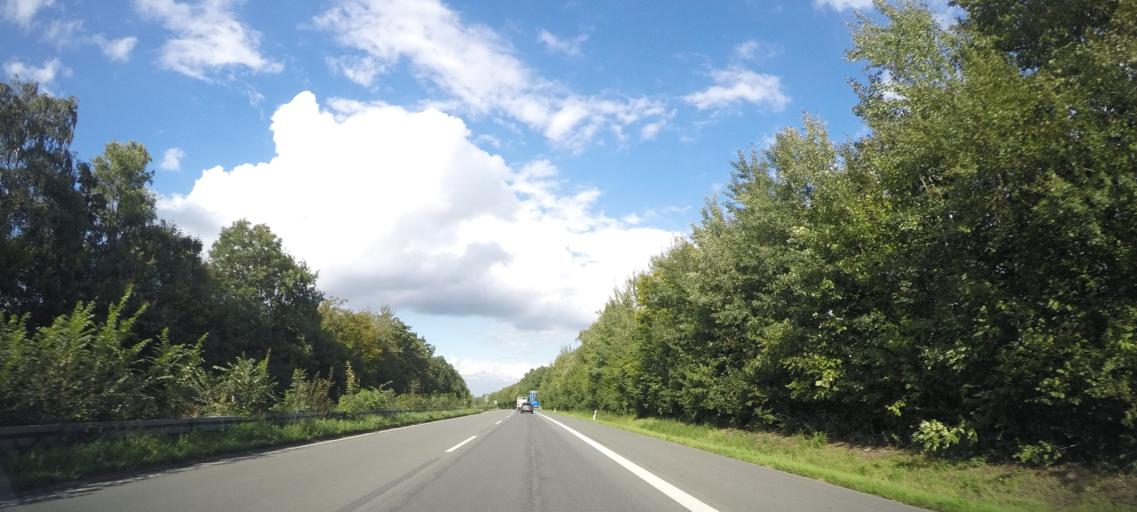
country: DE
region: North Rhine-Westphalia
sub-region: Regierungsbezirk Arnsberg
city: Unna
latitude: 51.5127
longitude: 7.7058
